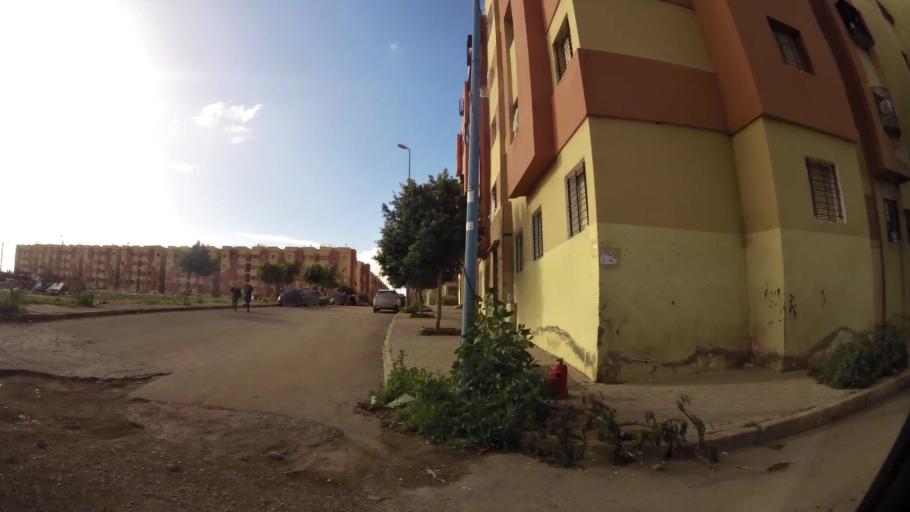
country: MA
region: Grand Casablanca
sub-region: Casablanca
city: Casablanca
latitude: 33.5498
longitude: -7.7026
